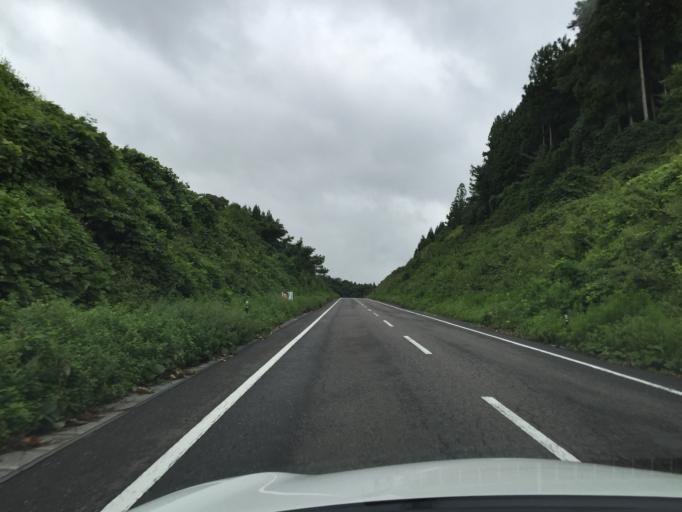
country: JP
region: Fukushima
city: Miharu
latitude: 37.4522
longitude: 140.5255
